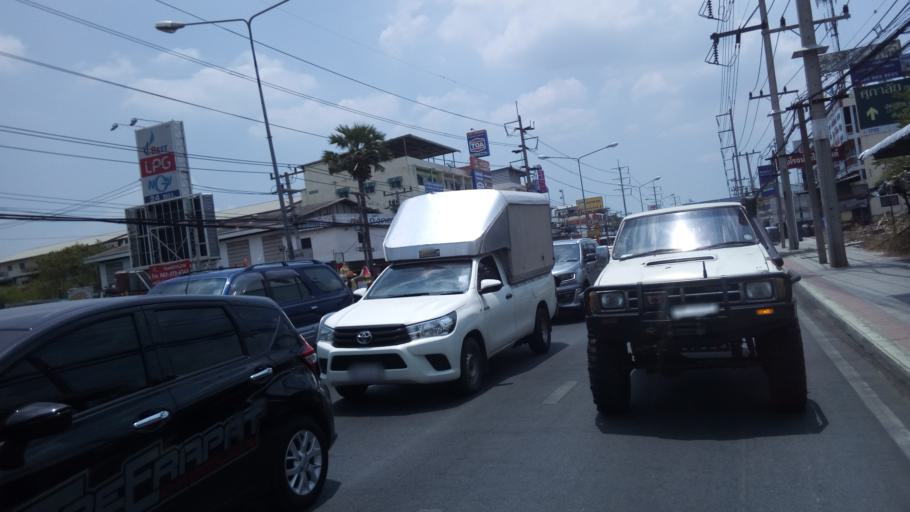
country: TH
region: Pathum Thani
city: Pathum Thani
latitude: 14.0290
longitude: 100.5253
